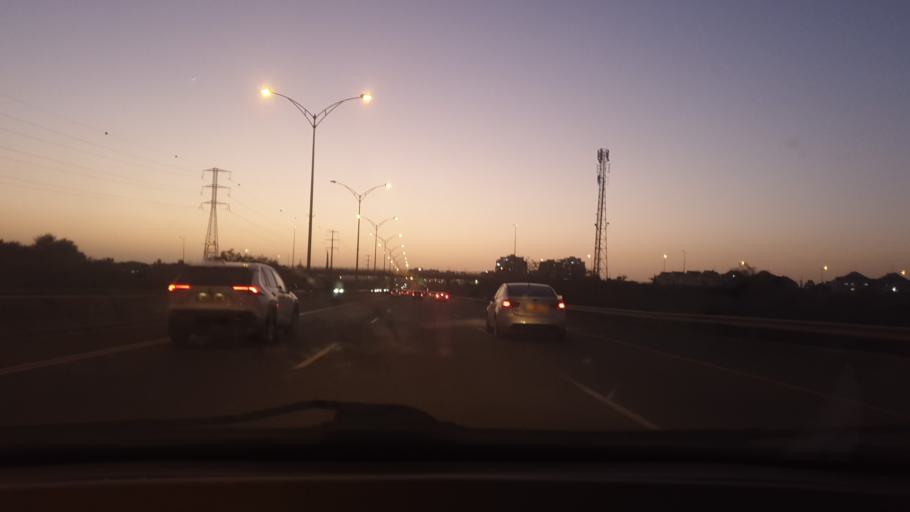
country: IL
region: Central District
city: Nehalim
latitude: 32.0681
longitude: 34.9231
